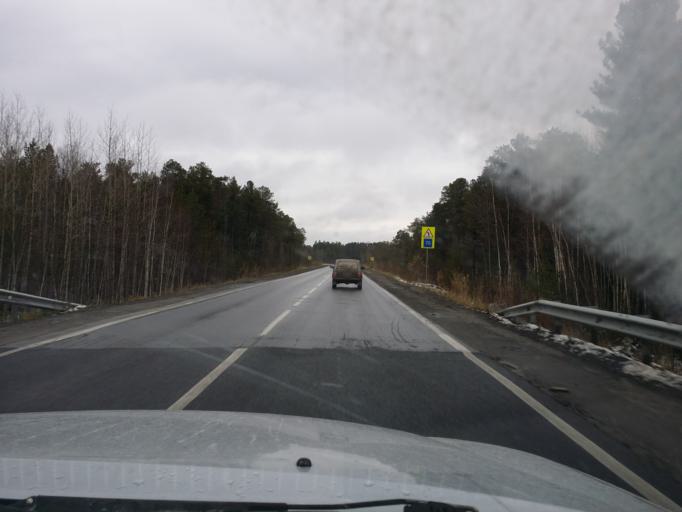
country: RU
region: Khanty-Mansiyskiy Avtonomnyy Okrug
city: Megion
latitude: 61.1192
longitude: 75.8368
